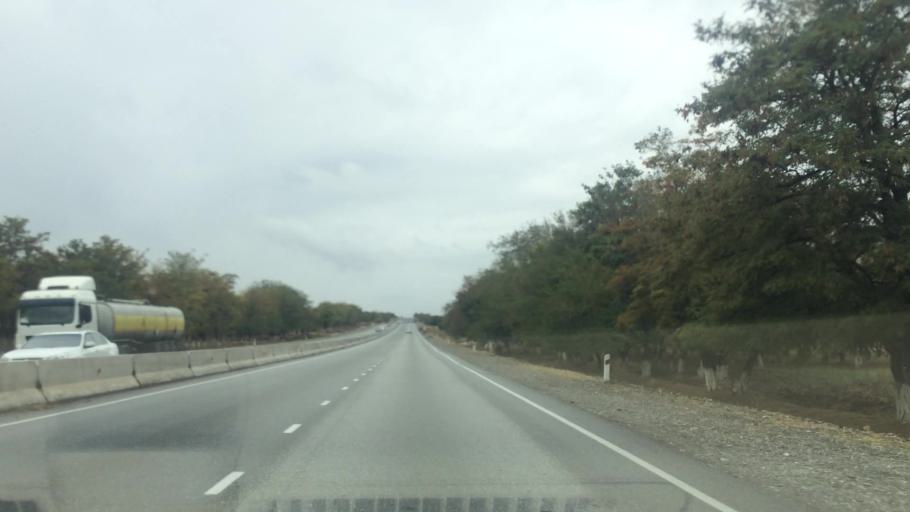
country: UZ
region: Samarqand
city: Bulung'ur
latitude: 39.8693
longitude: 67.4769
